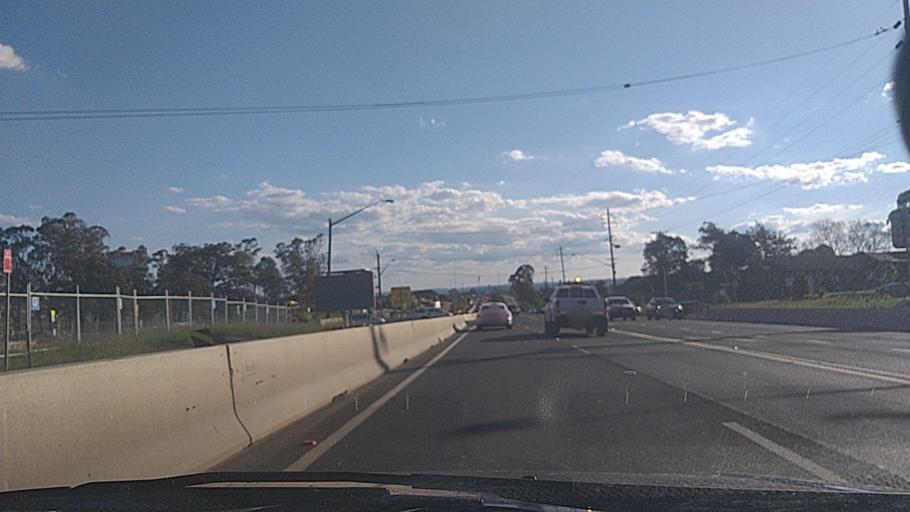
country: AU
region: New South Wales
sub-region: Penrith Municipality
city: Kingswood Park
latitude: -33.7815
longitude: 150.7092
